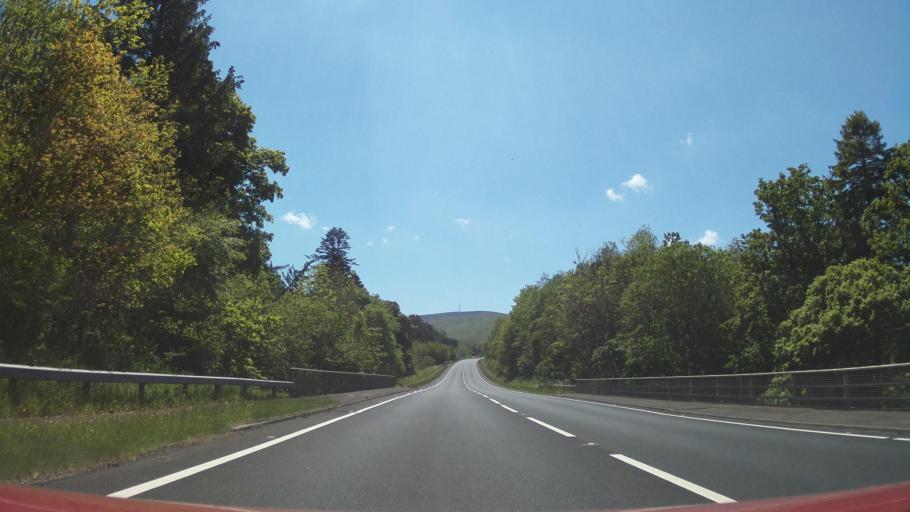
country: GB
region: Scotland
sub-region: The Scottish Borders
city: Hawick
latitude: 55.3374
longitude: -2.9392
